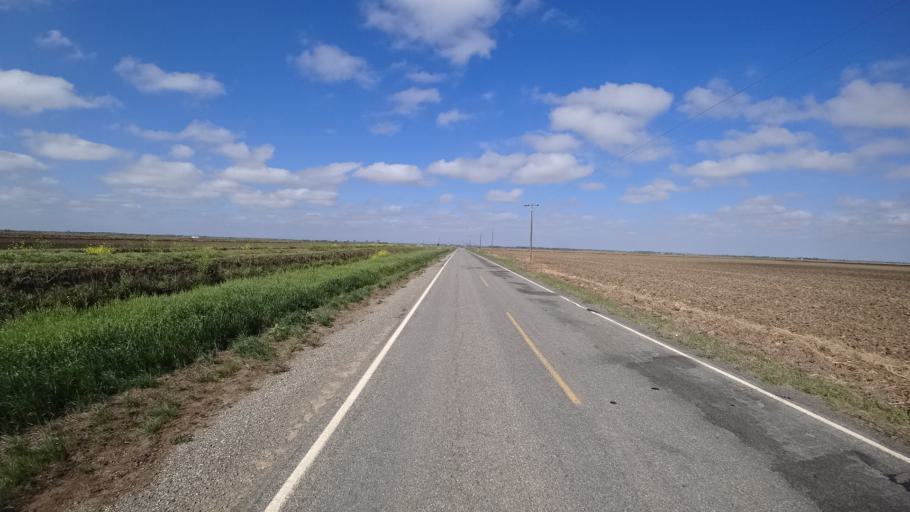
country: US
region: California
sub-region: Colusa County
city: Colusa
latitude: 39.3624
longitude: -121.9395
